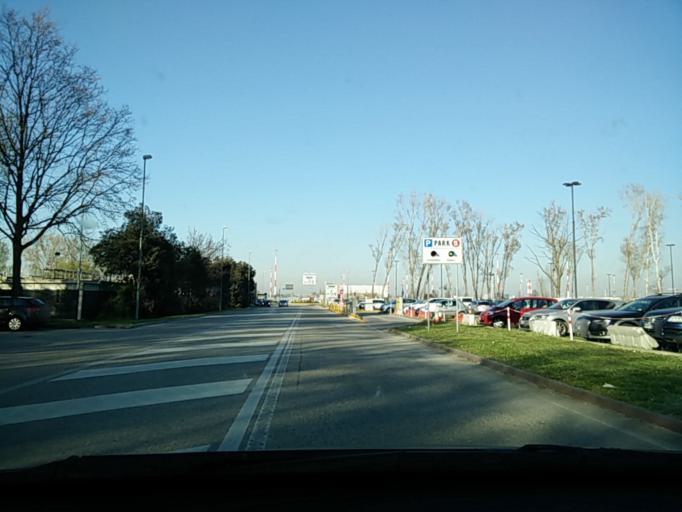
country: IT
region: Veneto
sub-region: Provincia di Venezia
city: Tessera
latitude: 45.5060
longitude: 12.3357
